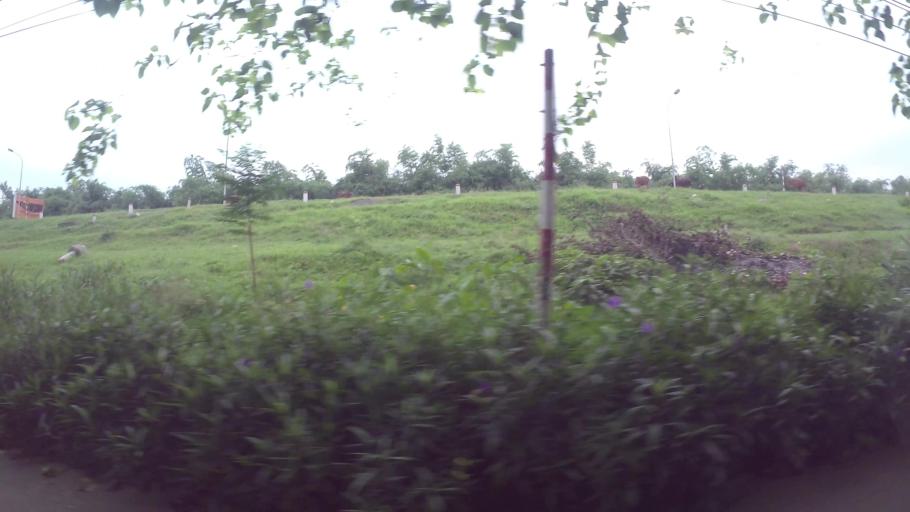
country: VN
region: Ha Noi
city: Trau Quy
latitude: 21.0456
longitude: 105.9289
